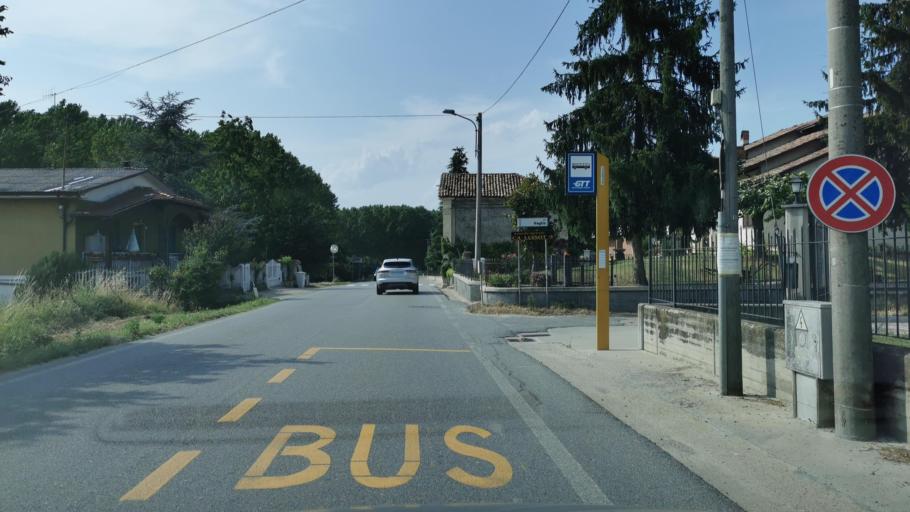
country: IT
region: Piedmont
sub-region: Provincia di Cuneo
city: Grinzane Cavour
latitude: 44.6466
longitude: 7.9967
